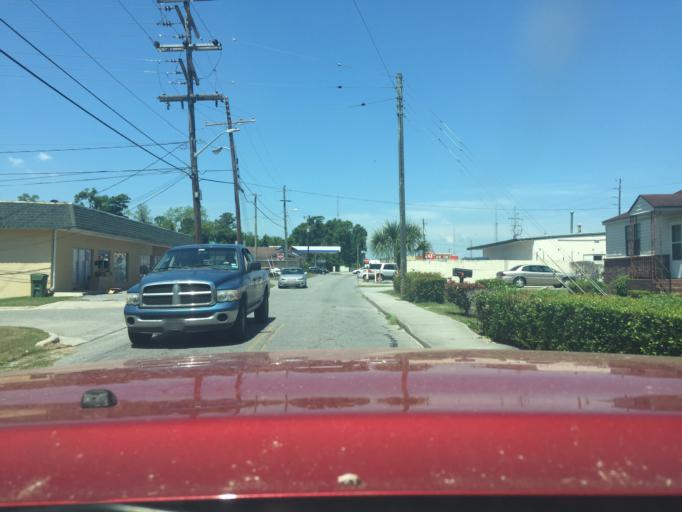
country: US
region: Georgia
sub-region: Chatham County
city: Thunderbolt
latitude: 32.0374
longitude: -81.0650
